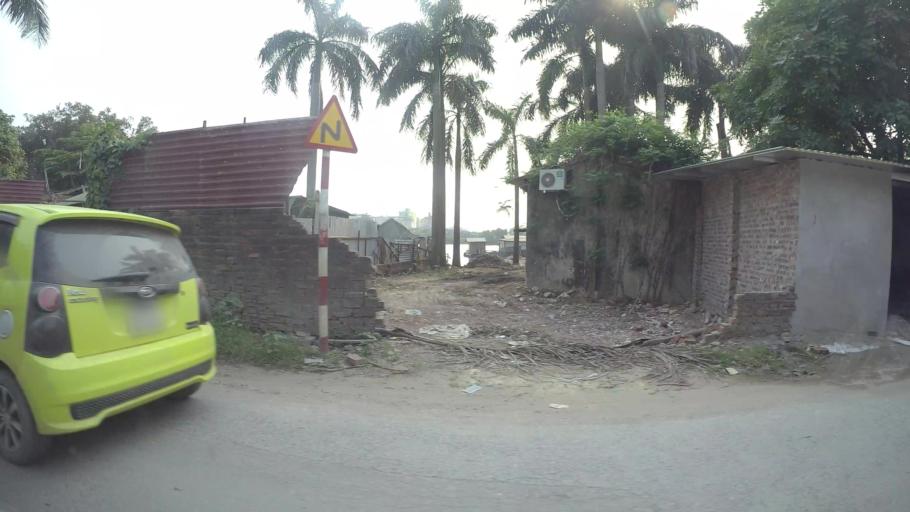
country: VN
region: Ha Noi
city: Ha Dong
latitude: 20.9967
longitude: 105.7437
